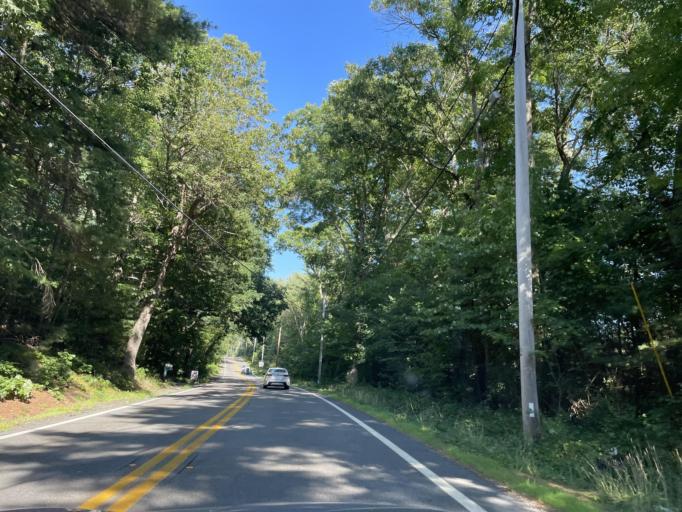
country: US
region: Massachusetts
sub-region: Worcester County
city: Douglas
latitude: 42.0530
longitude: -71.7474
